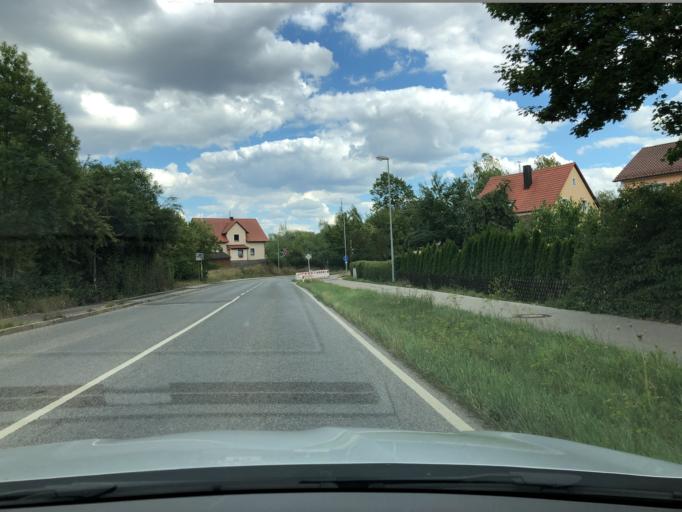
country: DE
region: Bavaria
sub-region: Upper Palatinate
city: Poppenricht
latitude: 49.4905
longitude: 11.7853
